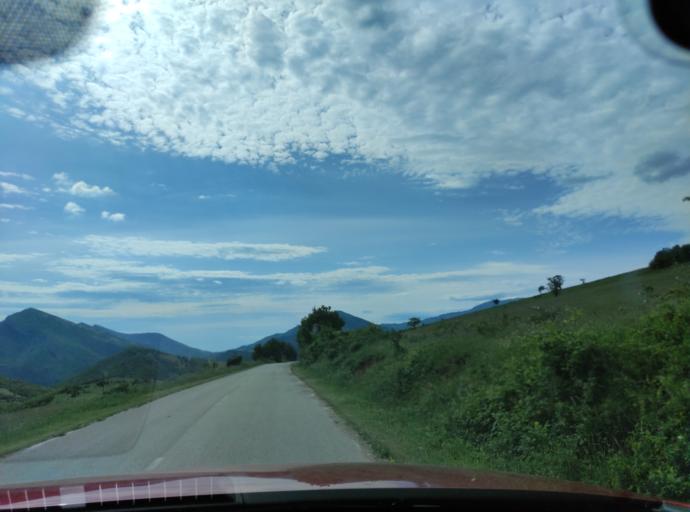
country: BG
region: Vidin
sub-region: Obshtina Belogradchik
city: Belogradchik
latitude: 43.5099
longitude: 22.7463
